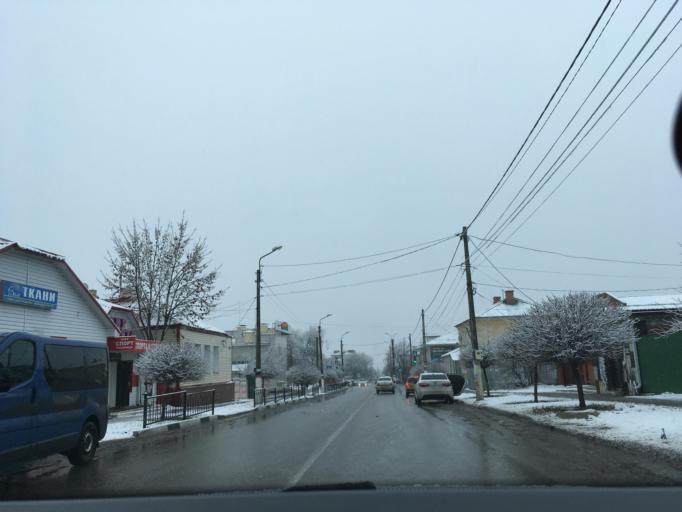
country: RU
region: Belgorod
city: Valuyki
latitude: 50.2140
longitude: 38.1015
